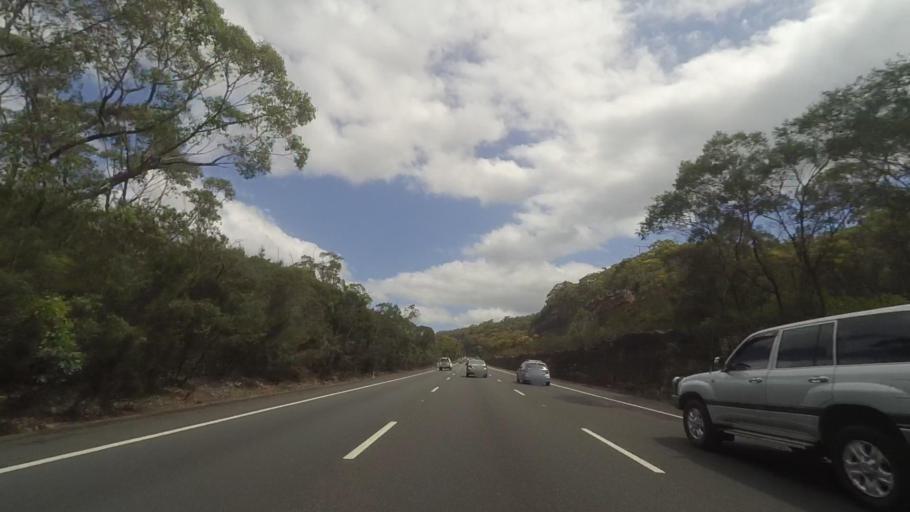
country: AU
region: New South Wales
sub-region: Hornsby Shire
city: Berowra
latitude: -33.5620
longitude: 151.1925
